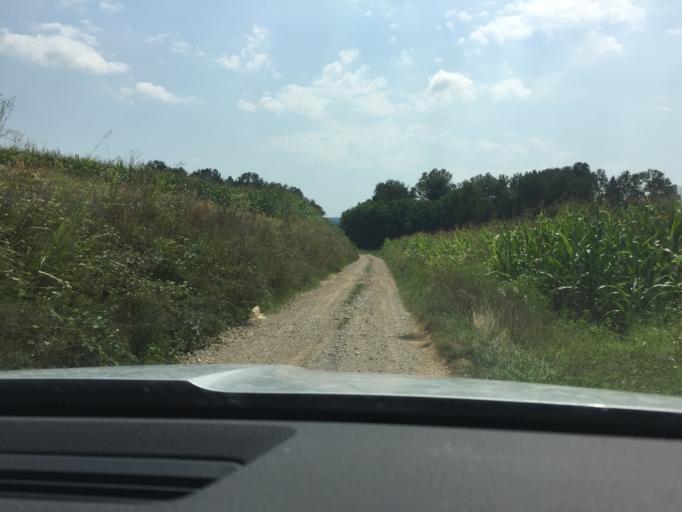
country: SI
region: Metlika
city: Metlika
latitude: 45.6552
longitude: 15.3461
